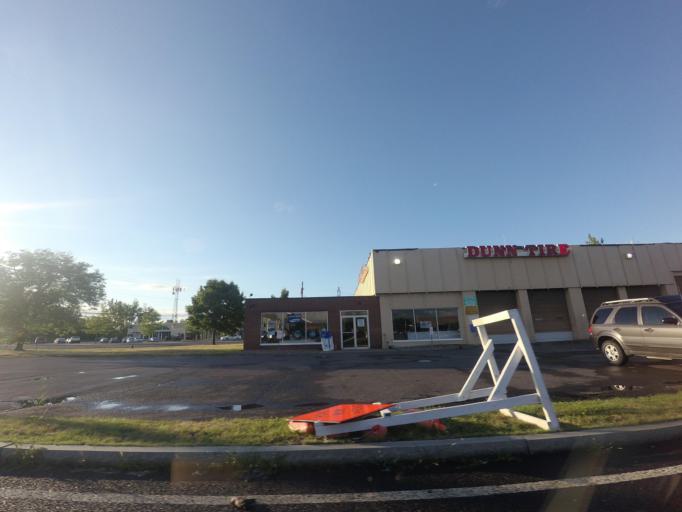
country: US
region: New York
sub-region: Onondaga County
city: East Syracuse
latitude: 43.0531
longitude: -76.0678
